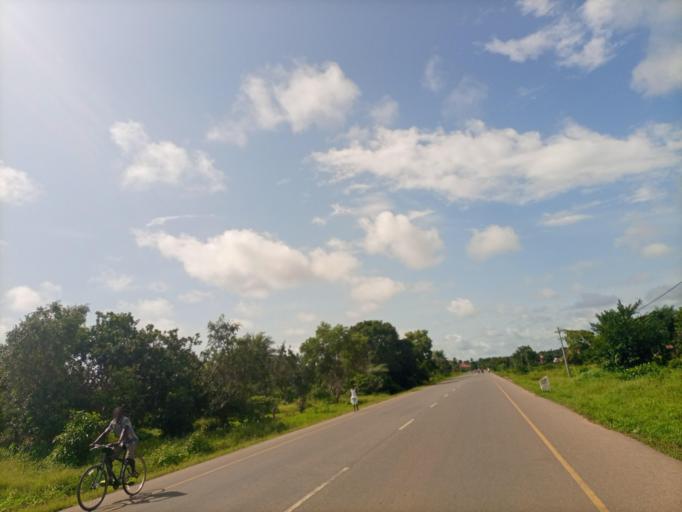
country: SL
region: Northern Province
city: Masoyila
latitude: 8.6119
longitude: -13.1758
